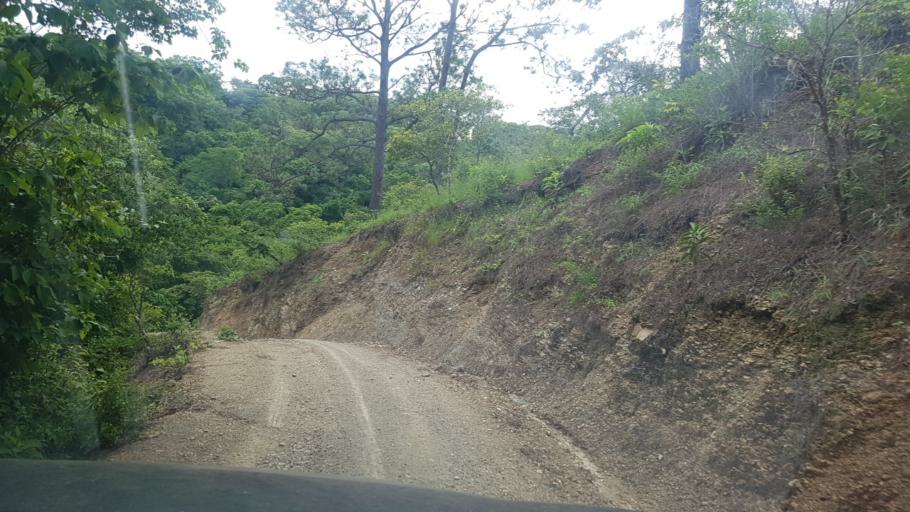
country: NI
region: Nueva Segovia
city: Ocotal
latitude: 13.5959
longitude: -86.4190
